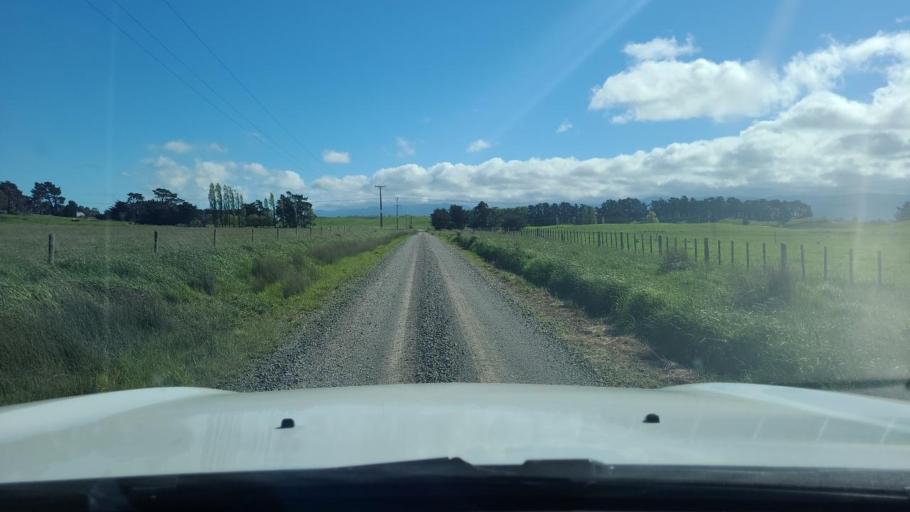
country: NZ
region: Wellington
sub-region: South Wairarapa District
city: Waipawa
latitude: -41.2006
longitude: 175.3600
